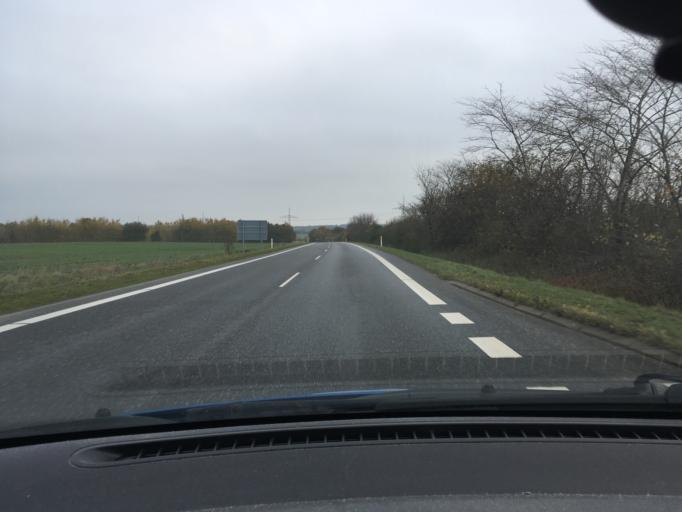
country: DK
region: South Denmark
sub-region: Aabenraa Kommune
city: Aabenraa
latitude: 54.9889
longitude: 9.4034
